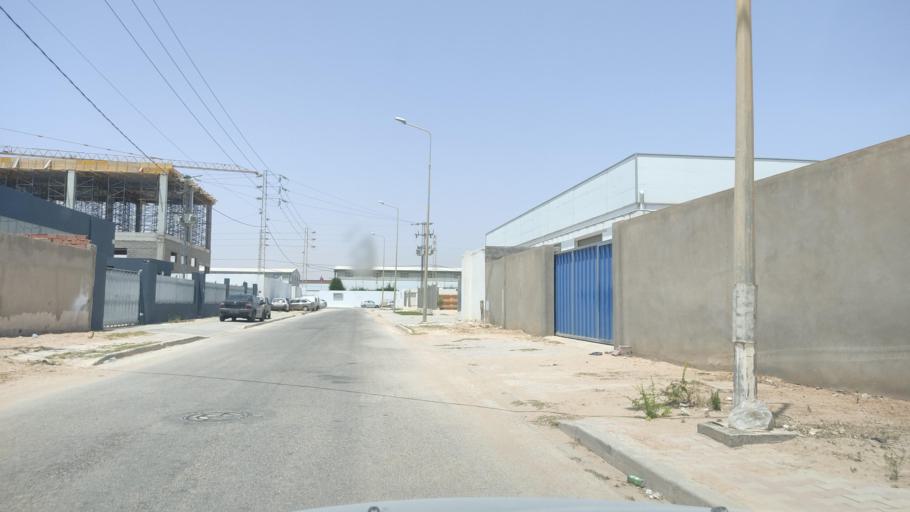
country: TN
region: Safaqis
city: Sfax
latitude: 34.6640
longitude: 10.6975
